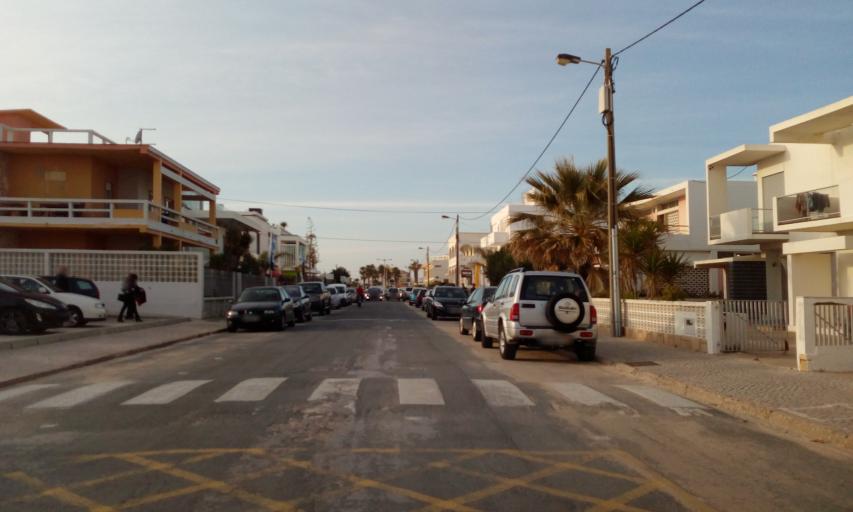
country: PT
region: Faro
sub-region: Faro
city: Faro
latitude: 37.0068
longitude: -7.9928
